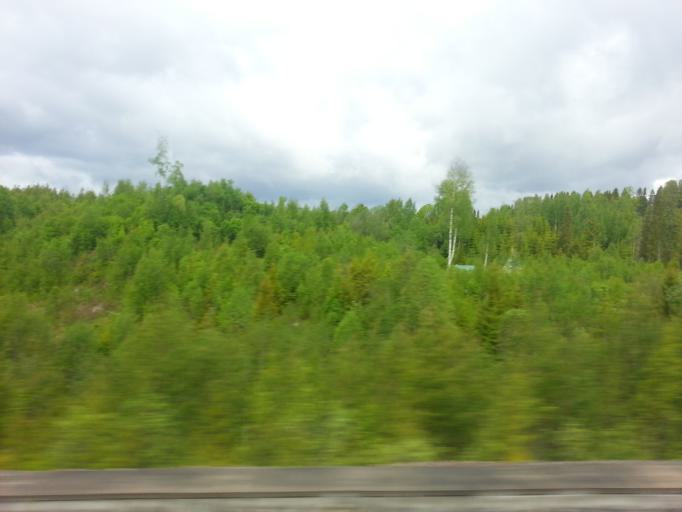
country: NO
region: Akershus
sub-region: Sorum
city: Frogner
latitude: 60.0172
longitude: 11.1155
